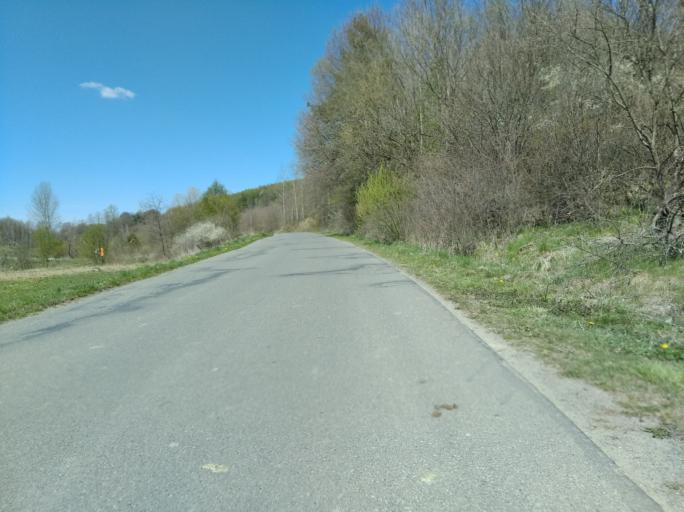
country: PL
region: Subcarpathian Voivodeship
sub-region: Powiat brzozowski
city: Dydnia
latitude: 49.7031
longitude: 22.1525
